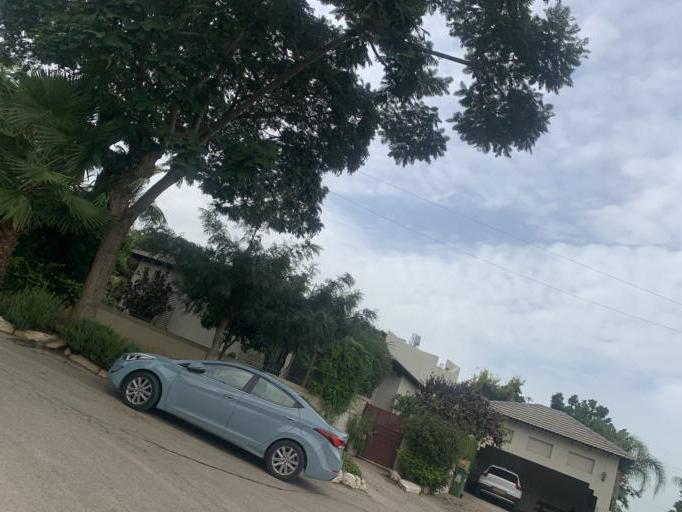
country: IL
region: Central District
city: Hod HaSharon
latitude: 32.1704
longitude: 34.8862
